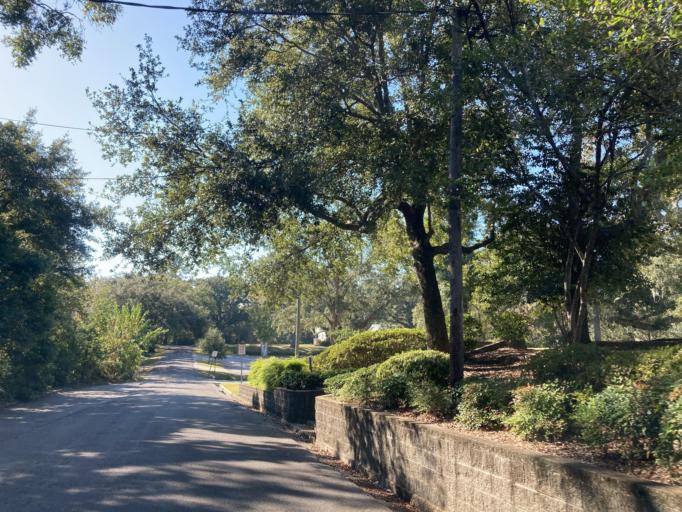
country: US
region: Mississippi
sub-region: Jackson County
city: Ocean Springs
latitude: 30.4078
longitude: -88.8288
